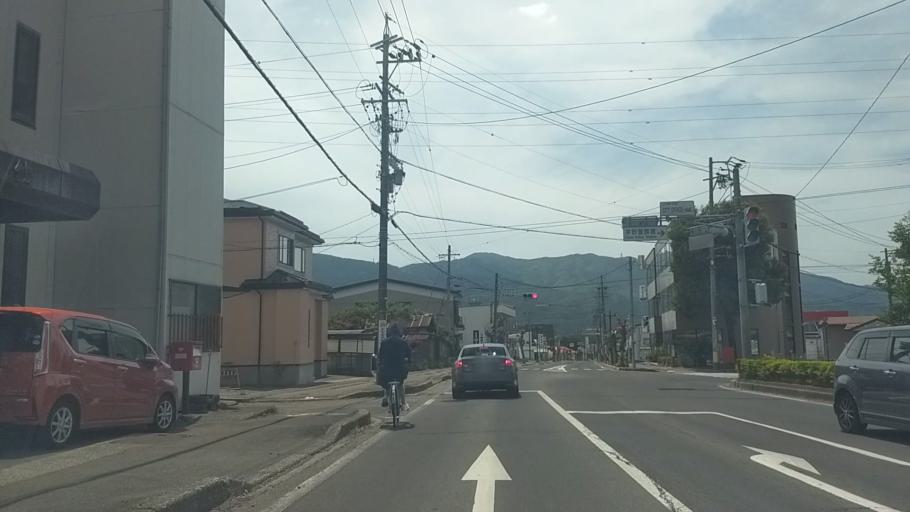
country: JP
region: Nagano
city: Chino
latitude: 35.9964
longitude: 138.1629
